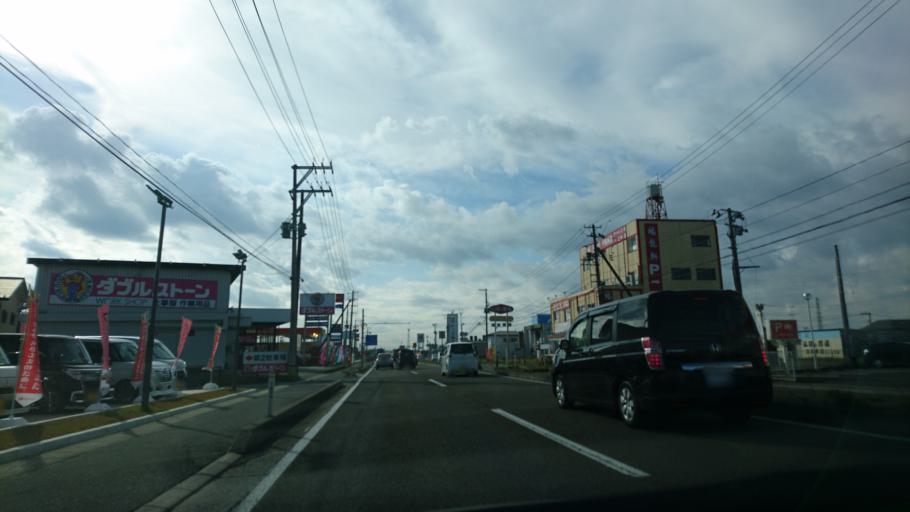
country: JP
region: Miyagi
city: Furukawa
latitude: 38.5771
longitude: 140.9460
